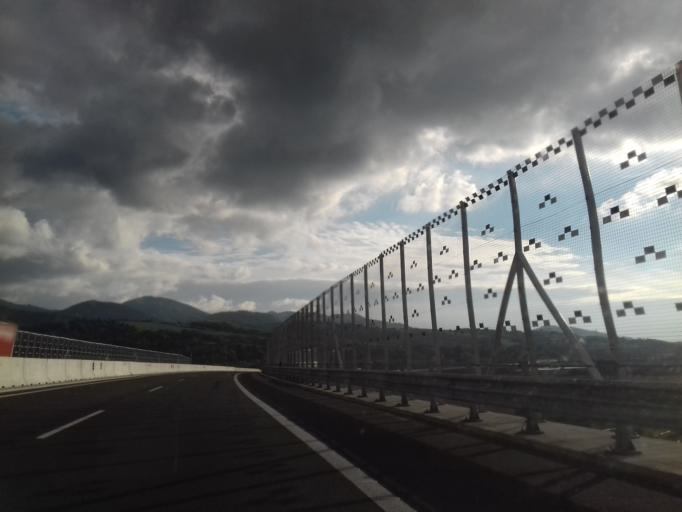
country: SK
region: Zilinsky
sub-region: Okres Zilina
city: Terchova
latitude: 49.1201
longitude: 19.0668
